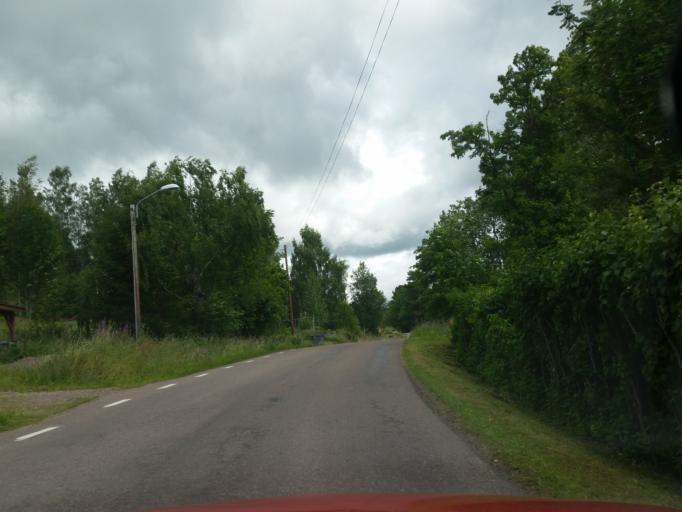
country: SE
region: Dalarna
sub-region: Leksand Municipality
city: Smedby
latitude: 60.7185
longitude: 15.0789
